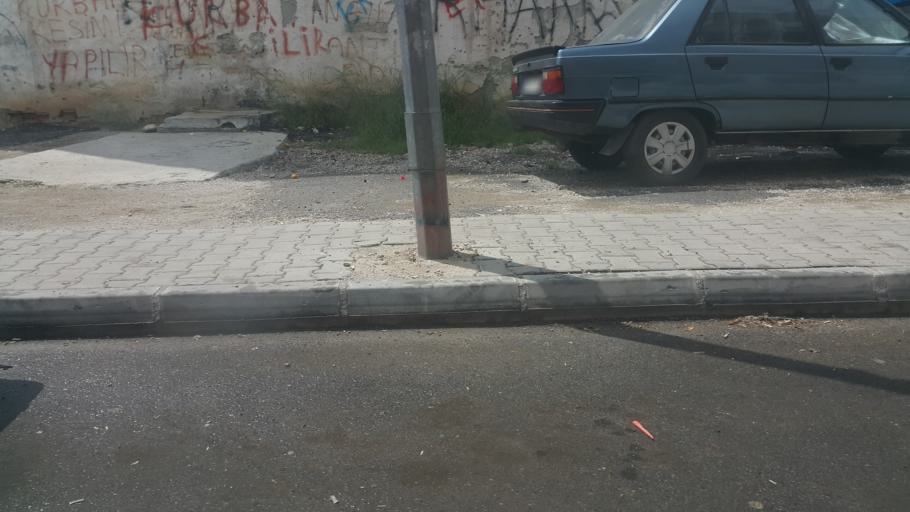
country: TR
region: Mersin
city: Mercin
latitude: 36.8036
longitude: 34.6284
